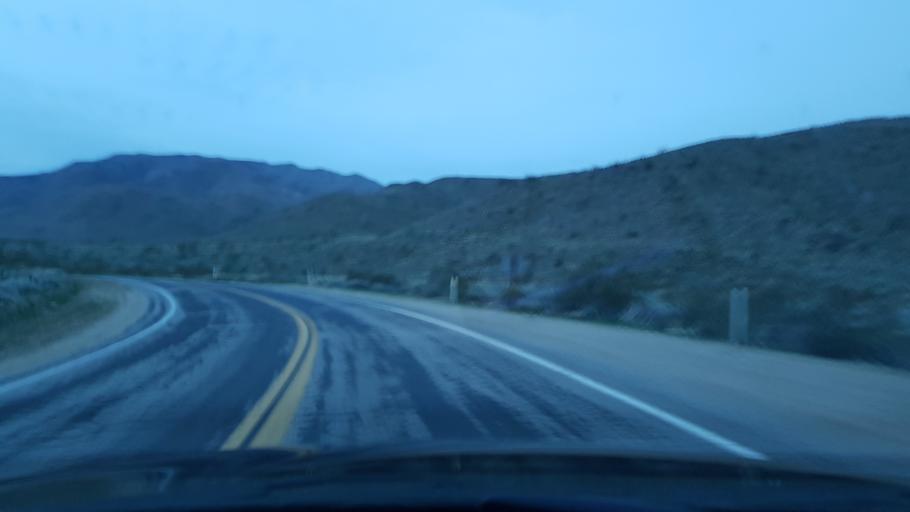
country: US
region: California
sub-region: San Diego County
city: Julian
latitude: 32.9979
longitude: -116.4476
